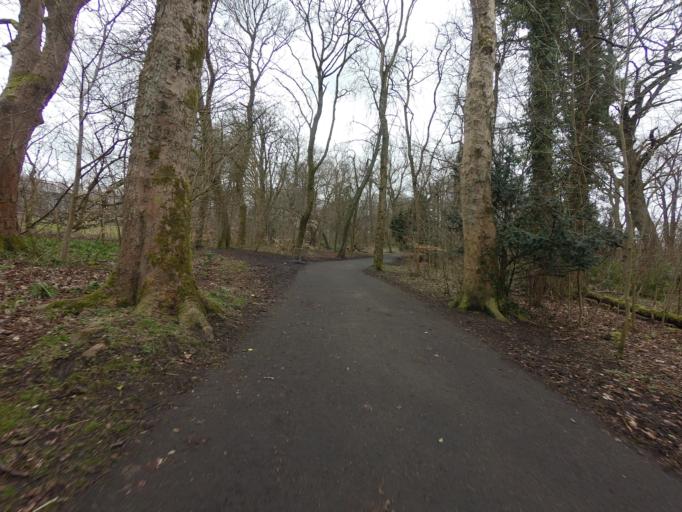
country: GB
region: Scotland
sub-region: East Renfrewshire
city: Giffnock
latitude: 55.8283
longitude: -4.3024
